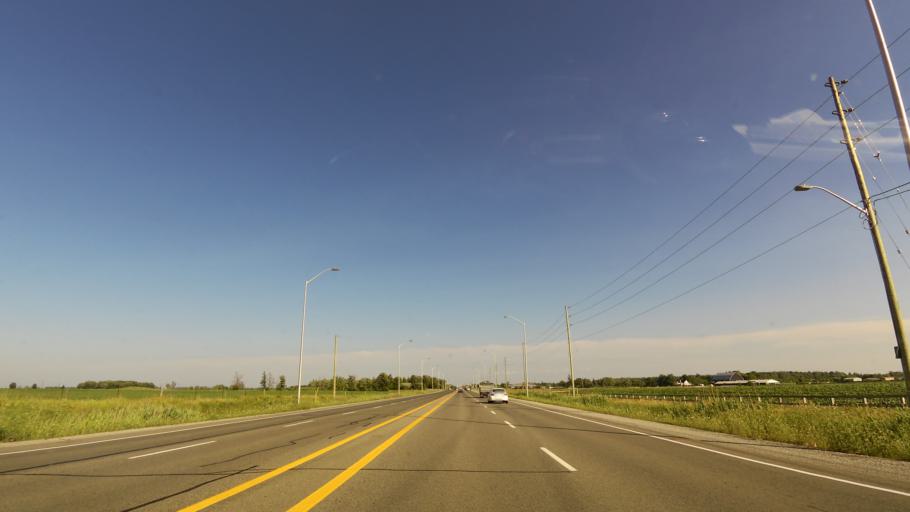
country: CA
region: Ontario
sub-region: Halton
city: Milton
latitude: 43.5591
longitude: -79.8134
